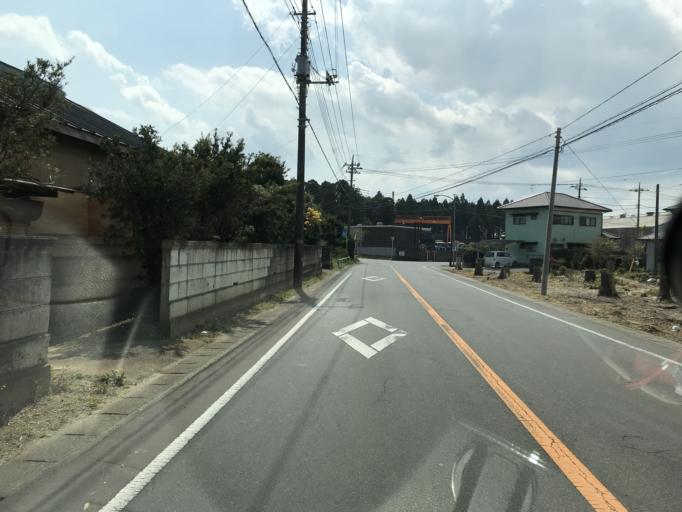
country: JP
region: Chiba
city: Omigawa
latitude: 35.8607
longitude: 140.5620
